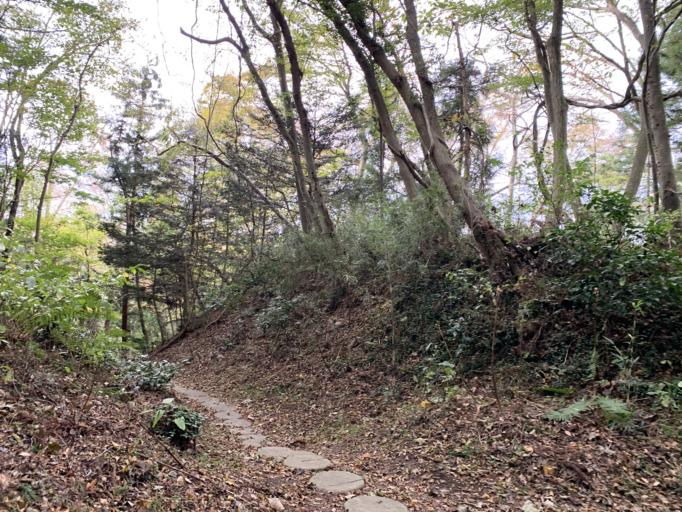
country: JP
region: Iwate
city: Mizusawa
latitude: 39.0262
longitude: 141.1357
